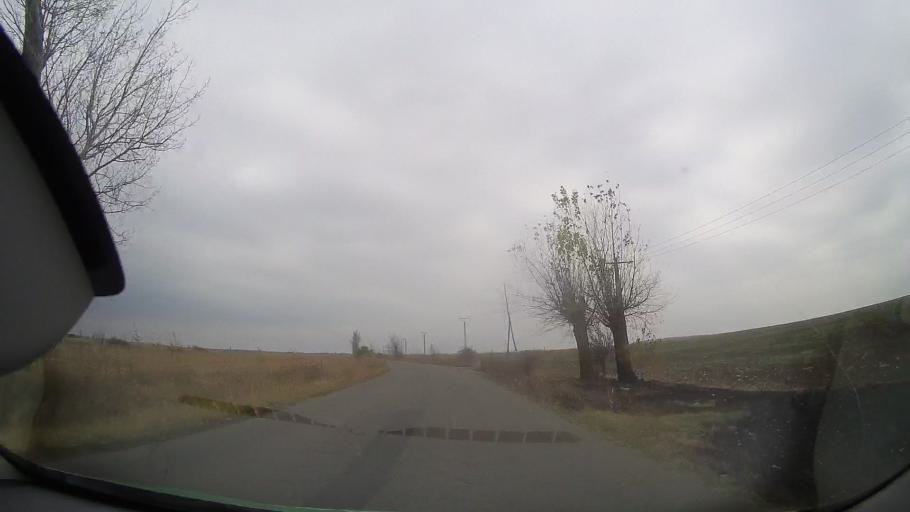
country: RO
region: Buzau
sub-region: Comuna Scutelnici
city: Scutelnici
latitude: 44.8744
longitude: 26.9391
